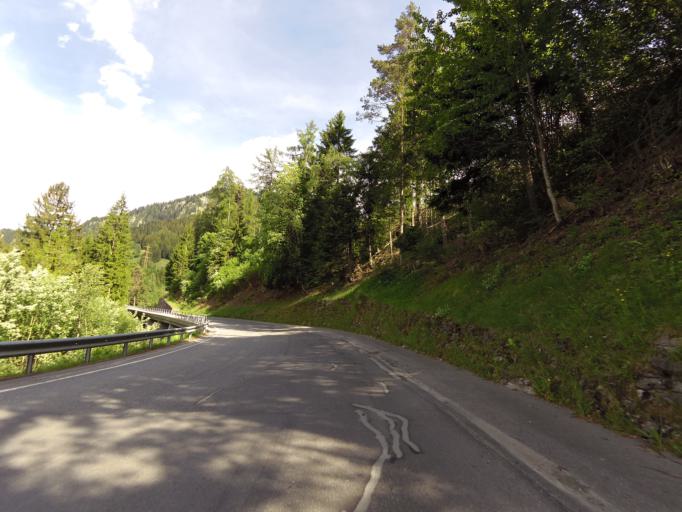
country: CH
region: Grisons
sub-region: Surselva District
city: Laax
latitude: 46.7881
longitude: 9.2882
